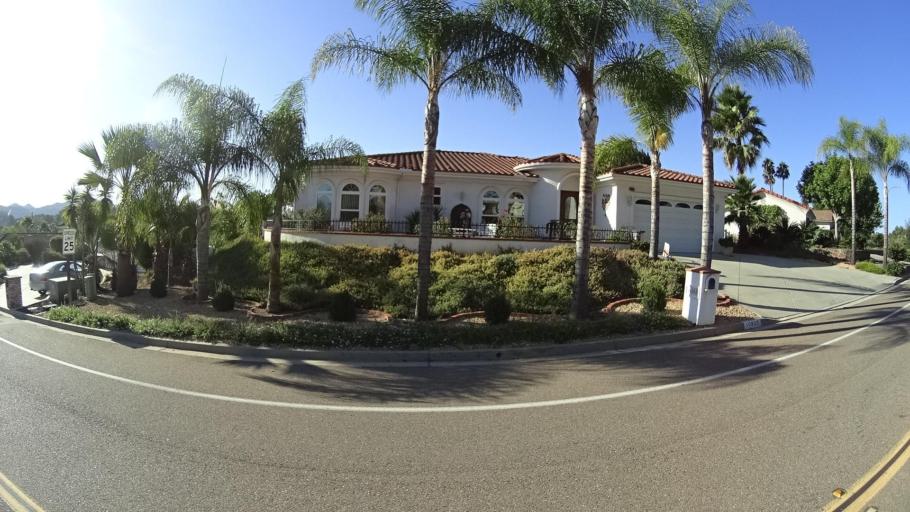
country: US
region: California
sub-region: San Diego County
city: Hidden Meadows
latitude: 33.2214
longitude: -117.1010
